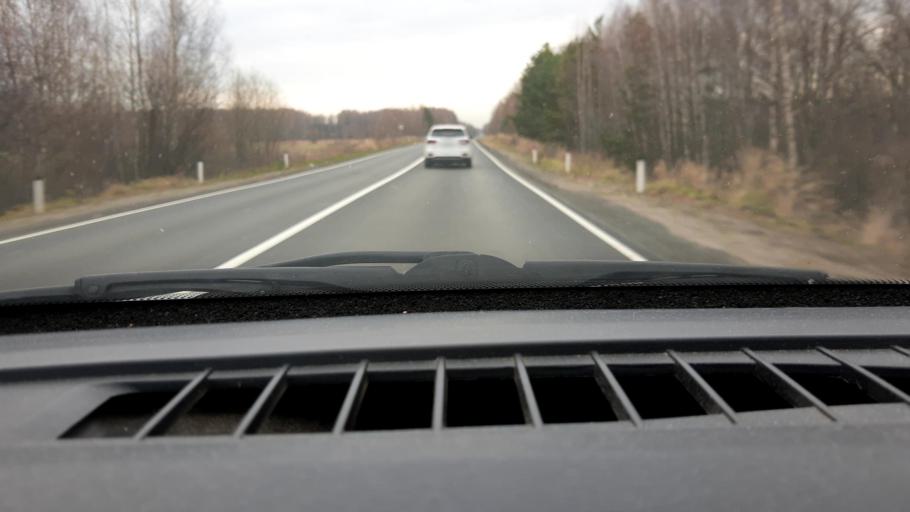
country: RU
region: Nizjnij Novgorod
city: Novaya Balakhna
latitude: 56.5739
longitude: 43.7040
